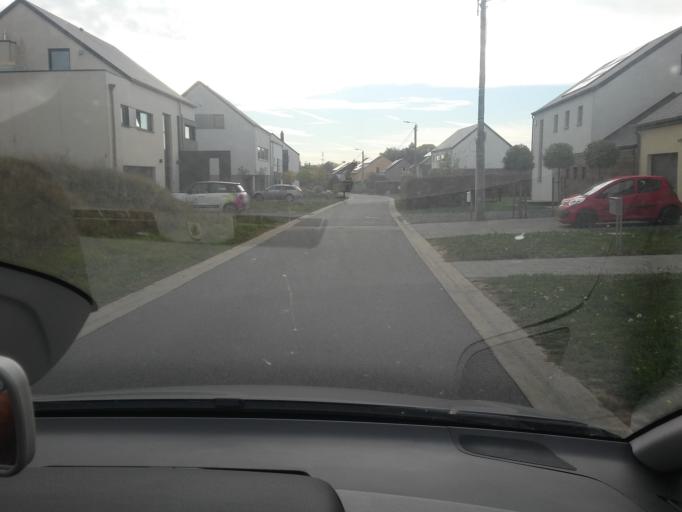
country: BE
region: Wallonia
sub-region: Province du Luxembourg
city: Attert
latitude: 49.7117
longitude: 5.7335
